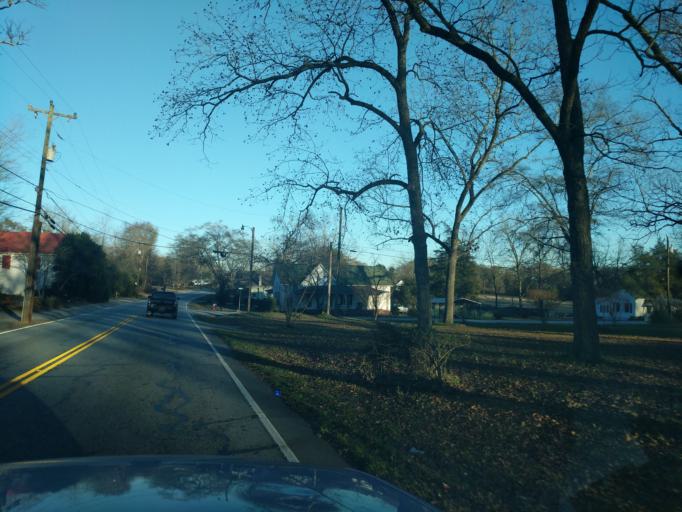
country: US
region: South Carolina
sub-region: Oconee County
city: Utica
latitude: 34.5646
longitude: -82.8965
